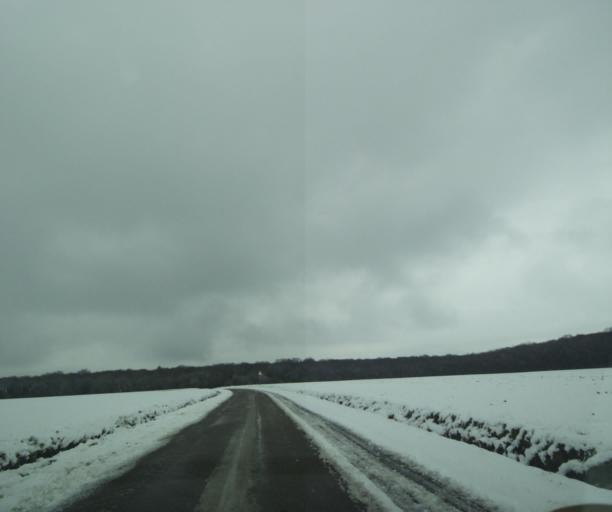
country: FR
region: Champagne-Ardenne
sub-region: Departement de la Haute-Marne
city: Laneuville-a-Remy
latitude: 48.3974
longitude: 4.8632
